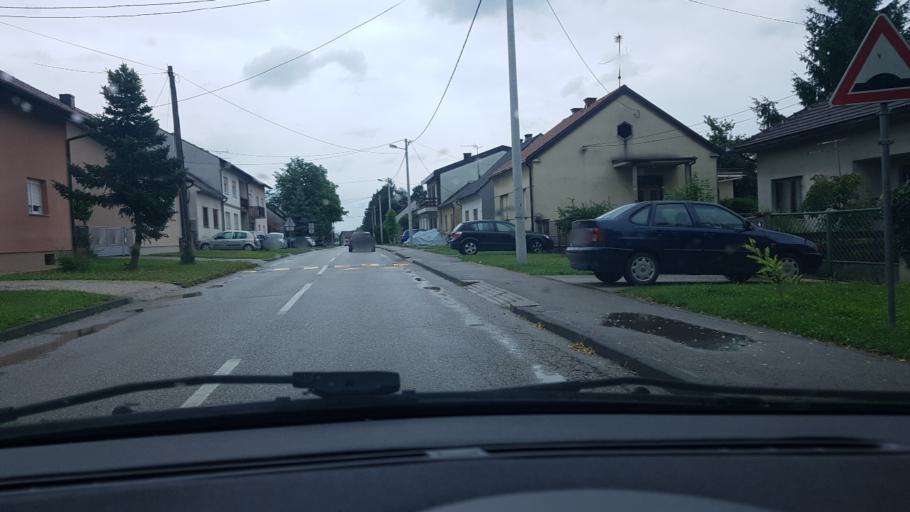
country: HR
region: Zagrebacka
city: Jastrebarsko
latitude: 45.6664
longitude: 15.6485
